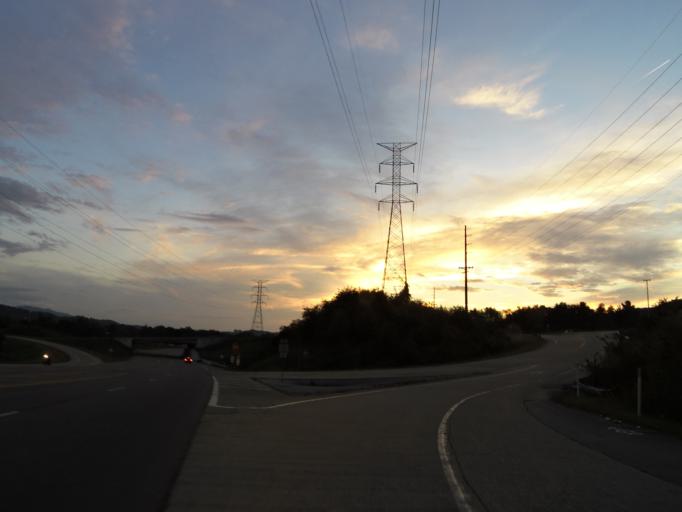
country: US
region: Tennessee
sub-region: Carter County
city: Elizabethton
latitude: 36.3592
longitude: -82.2024
